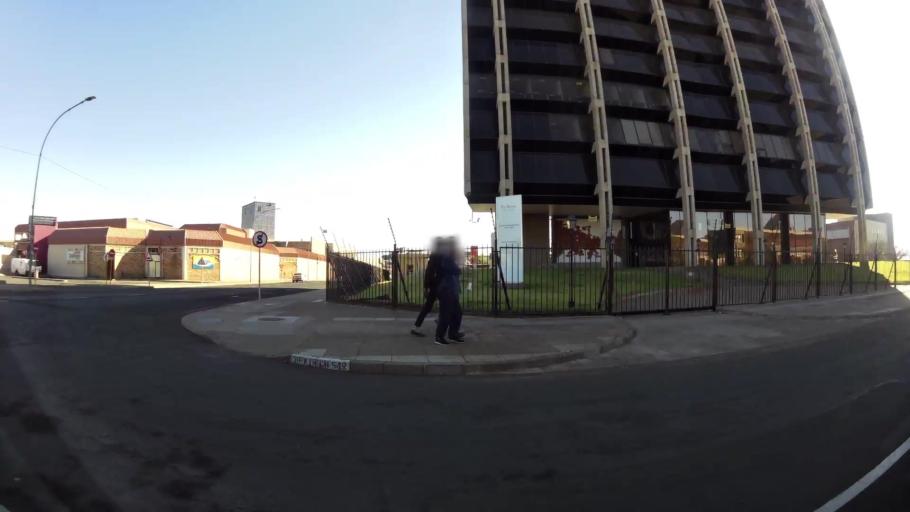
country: ZA
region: Northern Cape
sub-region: Frances Baard District Municipality
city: Kimberley
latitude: -28.7445
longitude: 24.7655
